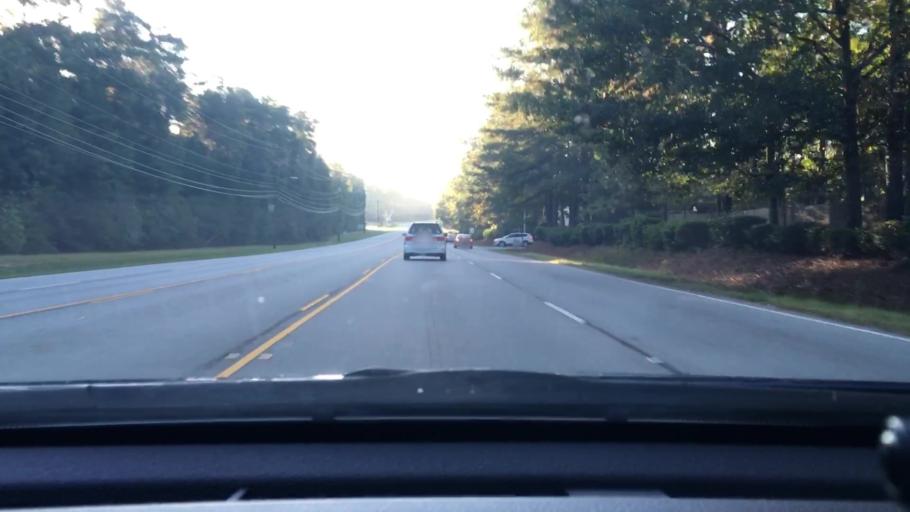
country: US
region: South Carolina
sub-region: Lexington County
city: Seven Oaks
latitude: 34.0815
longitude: -81.1339
